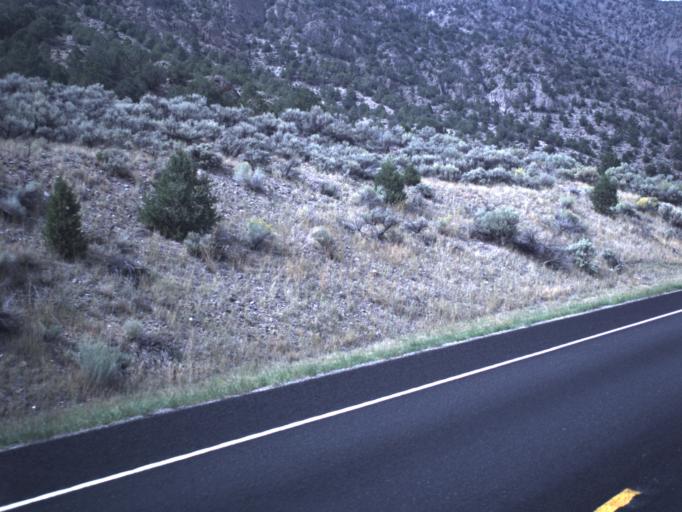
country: US
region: Utah
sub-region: Piute County
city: Junction
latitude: 38.0806
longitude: -112.3400
